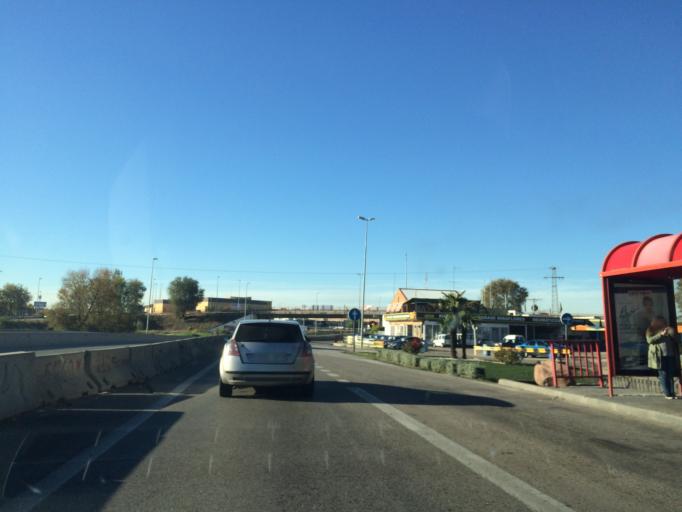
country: ES
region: Madrid
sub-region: Provincia de Madrid
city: Mostoles
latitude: 40.3140
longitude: -3.8394
